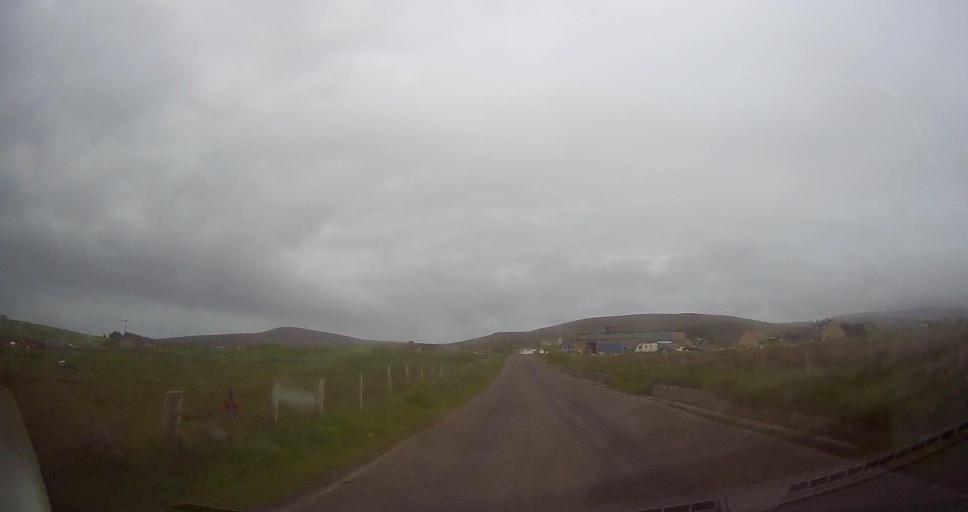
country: GB
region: Scotland
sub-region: Orkney Islands
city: Stromness
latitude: 58.8315
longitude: -3.2008
